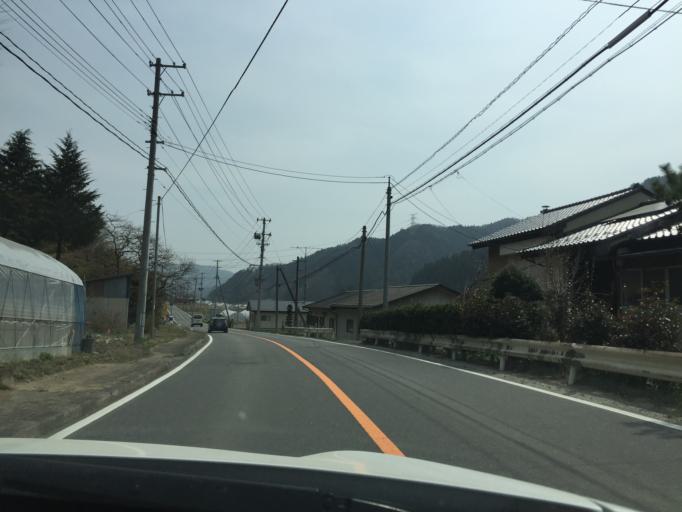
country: JP
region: Fukushima
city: Ishikawa
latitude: 37.1098
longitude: 140.5054
